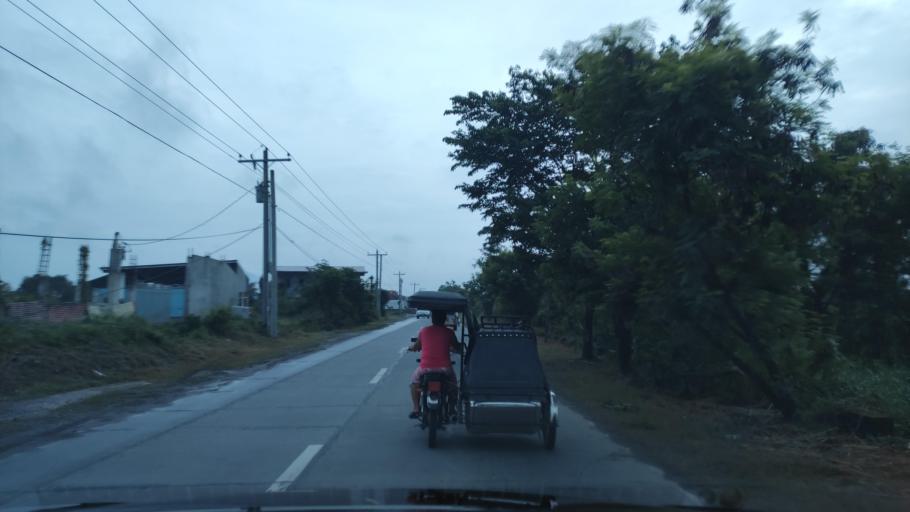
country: PH
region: Central Luzon
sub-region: Province of Pampanga
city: Santo Domingo
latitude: 15.0655
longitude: 120.7555
